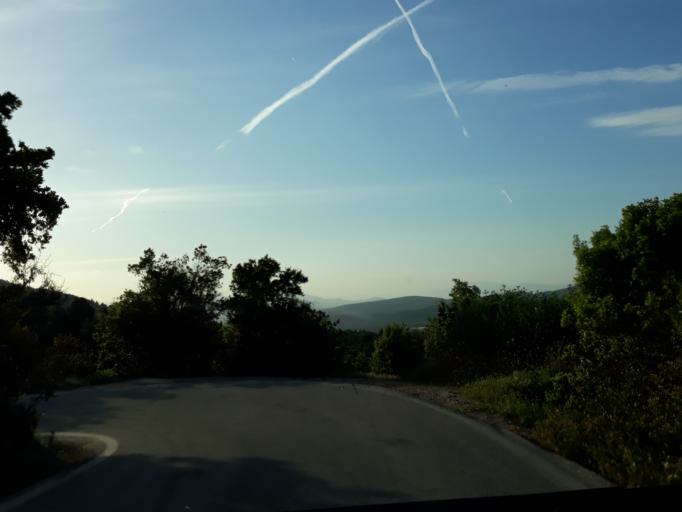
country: GR
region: Attica
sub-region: Nomarchia Anatolikis Attikis
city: Afidnes
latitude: 38.2271
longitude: 23.7904
